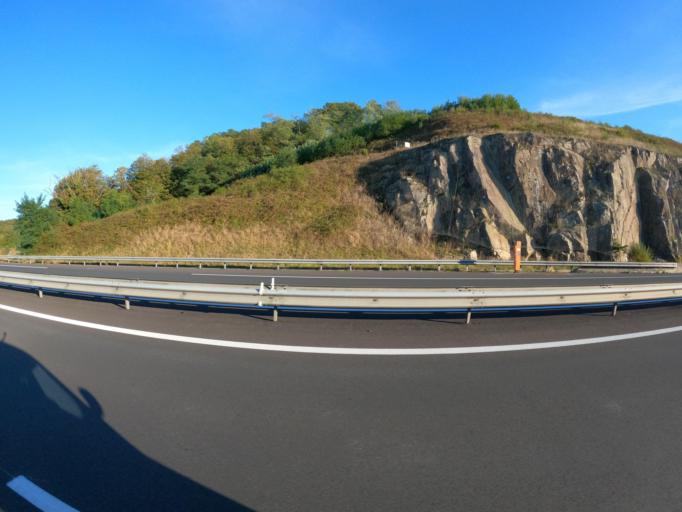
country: FR
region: Pays de la Loire
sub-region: Departement de la Vendee
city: Saint-Laurent-sur-Sevre
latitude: 46.9638
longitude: -0.9235
